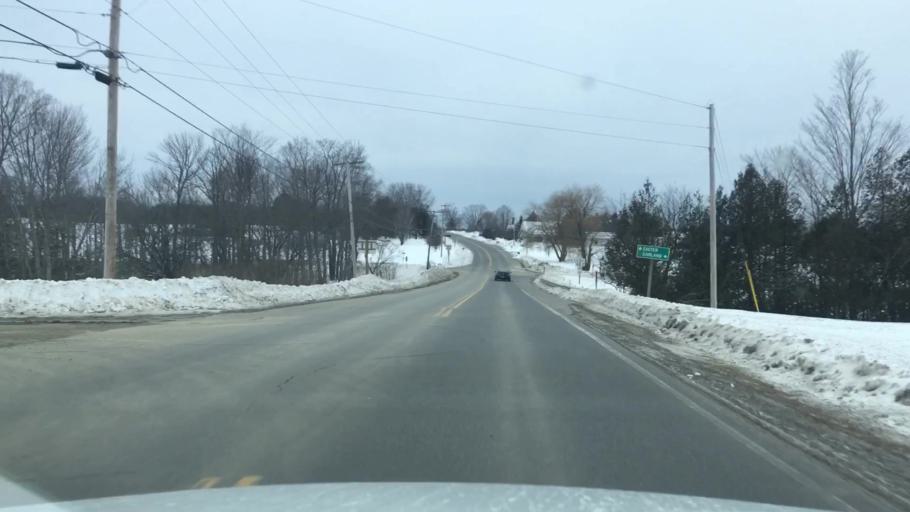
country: US
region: Maine
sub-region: Penobscot County
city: Charleston
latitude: 44.9955
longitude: -69.0515
